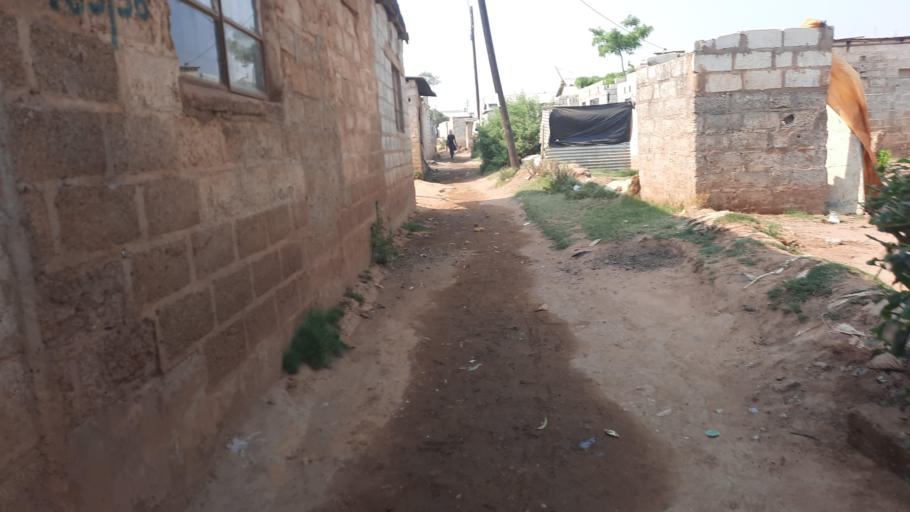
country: ZM
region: Lusaka
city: Lusaka
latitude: -15.3992
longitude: 28.3822
